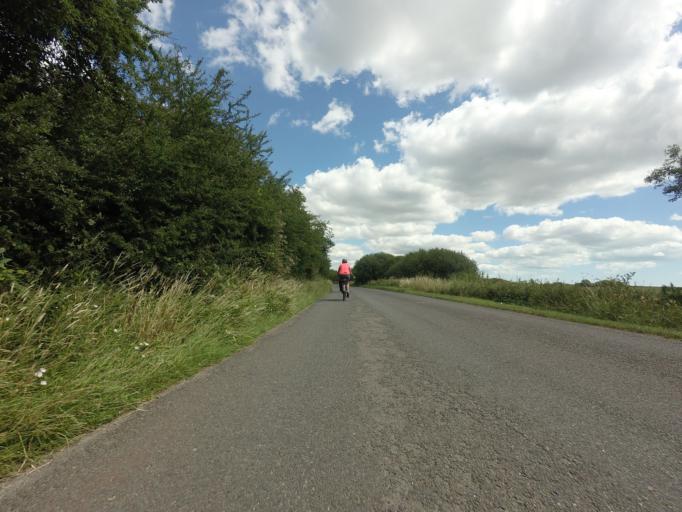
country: GB
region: England
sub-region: East Sussex
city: Hailsham
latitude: 50.8391
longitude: 0.1768
